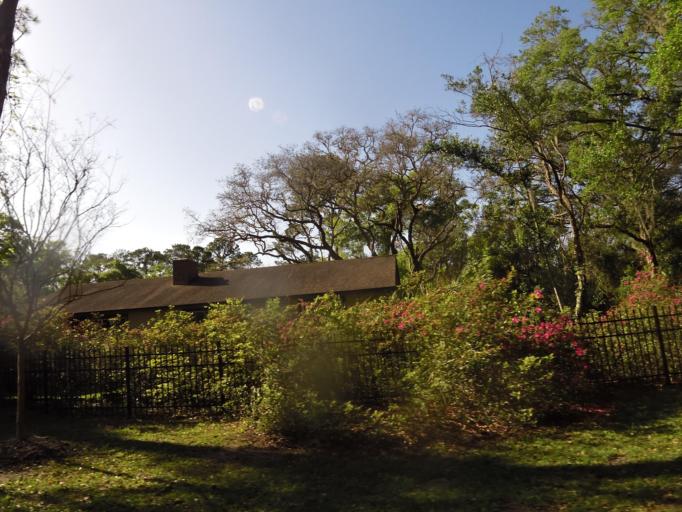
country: US
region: Florida
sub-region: Duval County
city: Jacksonville
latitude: 30.2770
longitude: -81.5843
